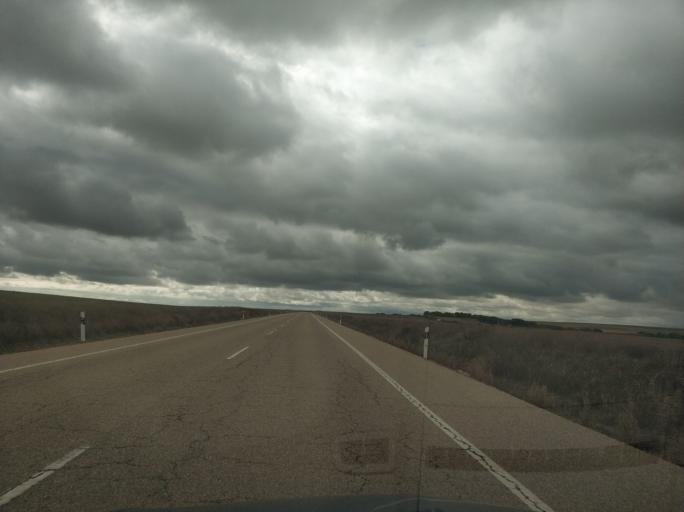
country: ES
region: Castille and Leon
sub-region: Provincia de Valladolid
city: Alaejos
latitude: 41.2748
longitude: -5.2533
